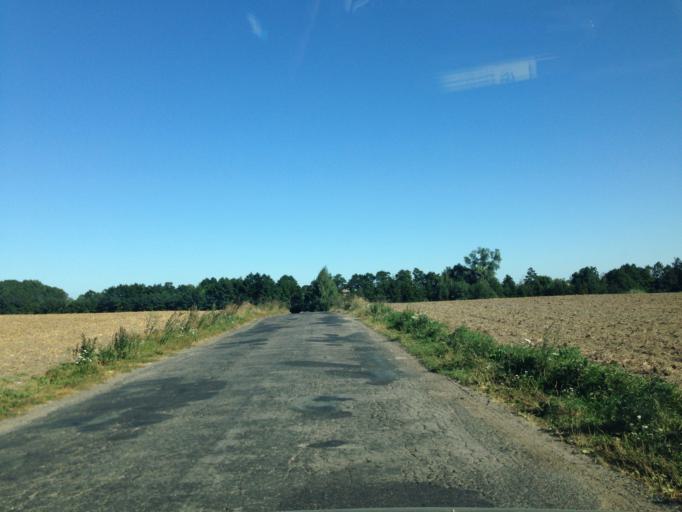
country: PL
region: Kujawsko-Pomorskie
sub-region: Powiat brodnicki
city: Swiedziebnia
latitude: 53.2019
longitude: 19.5473
